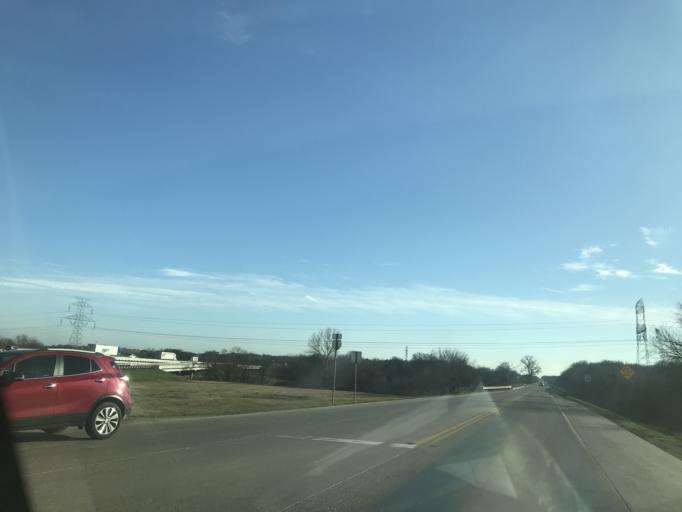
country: US
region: Texas
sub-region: Ellis County
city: Ferris
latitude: 32.5607
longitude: -96.6658
